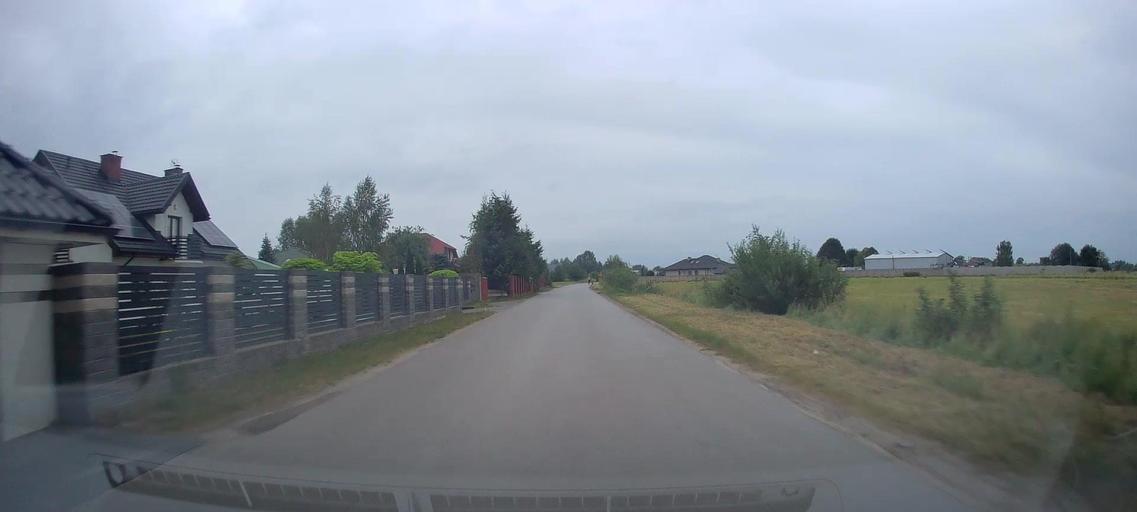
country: PL
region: Masovian Voivodeship
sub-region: Powiat radomski
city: Jedlinsk
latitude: 51.4743
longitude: 21.1227
